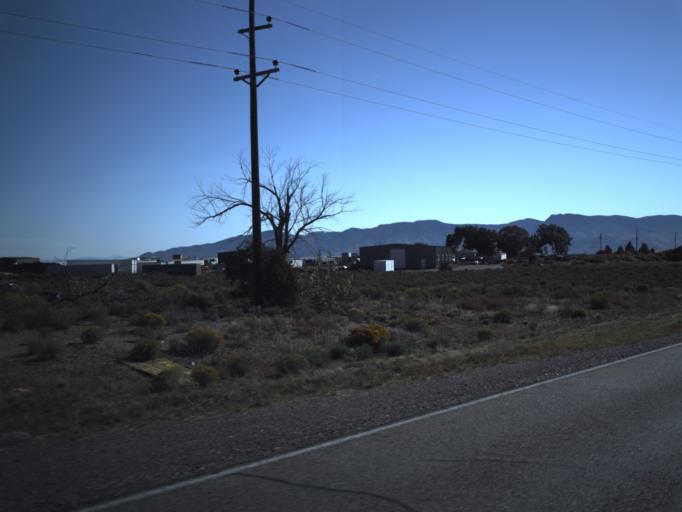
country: US
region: Utah
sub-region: Washington County
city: Enterprise
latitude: 37.7064
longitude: -113.6476
